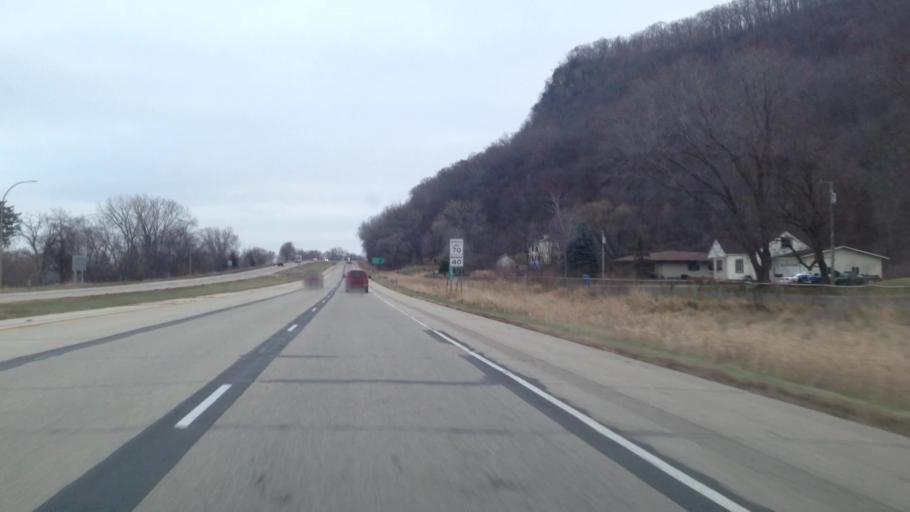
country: US
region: Wisconsin
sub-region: La Crosse County
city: Brice Prairie
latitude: 43.9081
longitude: -91.3559
